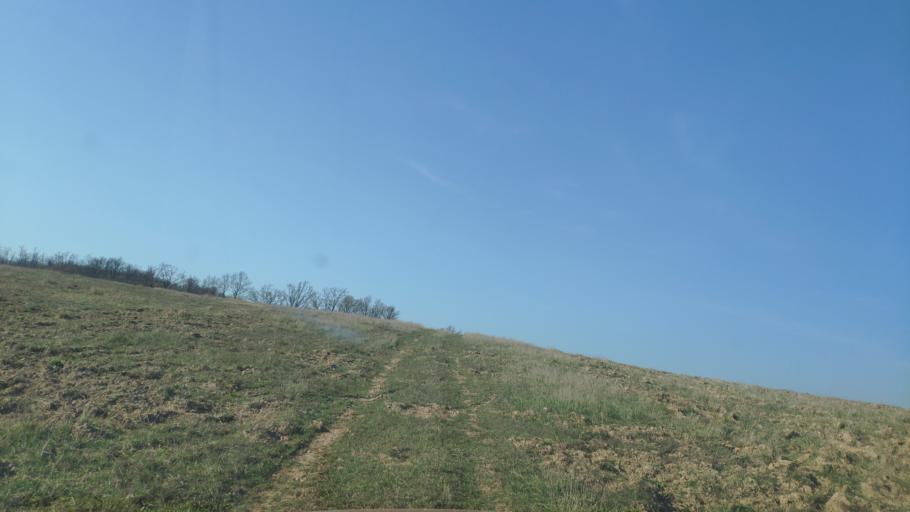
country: SK
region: Banskobystricky
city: Revuca
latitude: 48.5421
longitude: 20.2569
